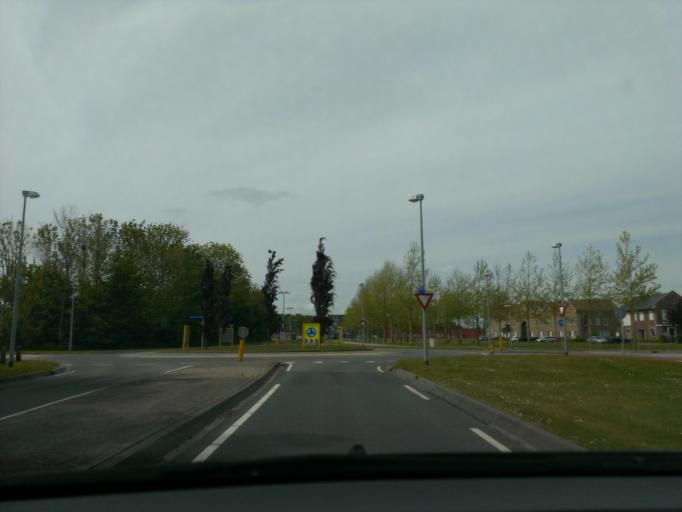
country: NL
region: Flevoland
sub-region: Gemeente Almere
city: Almere Stad
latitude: 52.4031
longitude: 5.3112
